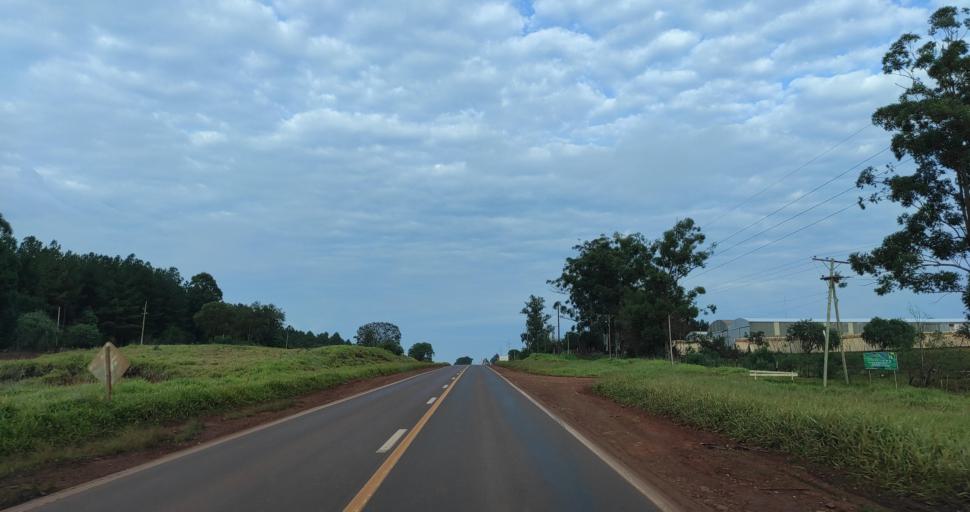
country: AR
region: Corrientes
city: Gobernador Ingeniero Valentin Virasoro
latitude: -27.9440
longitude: -55.9864
